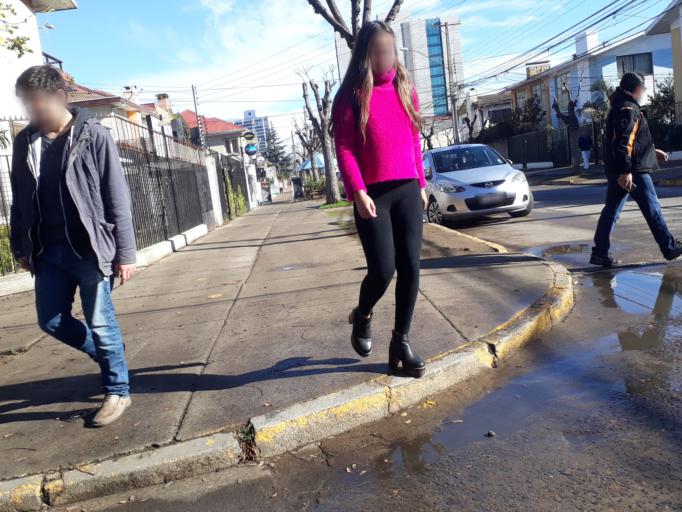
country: CL
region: Valparaiso
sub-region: Provincia de Valparaiso
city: Vina del Mar
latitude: -33.0118
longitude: -71.5454
